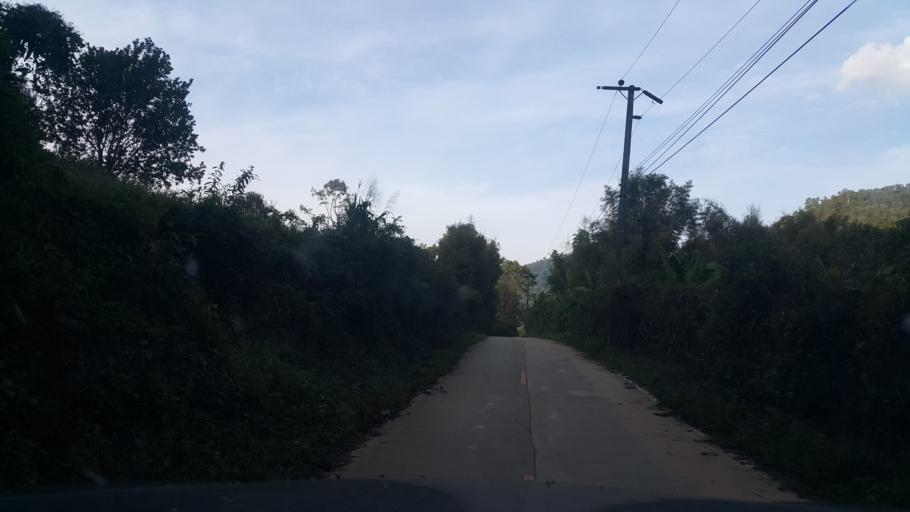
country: TH
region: Chiang Mai
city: Samoeng
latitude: 19.0078
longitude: 98.6721
